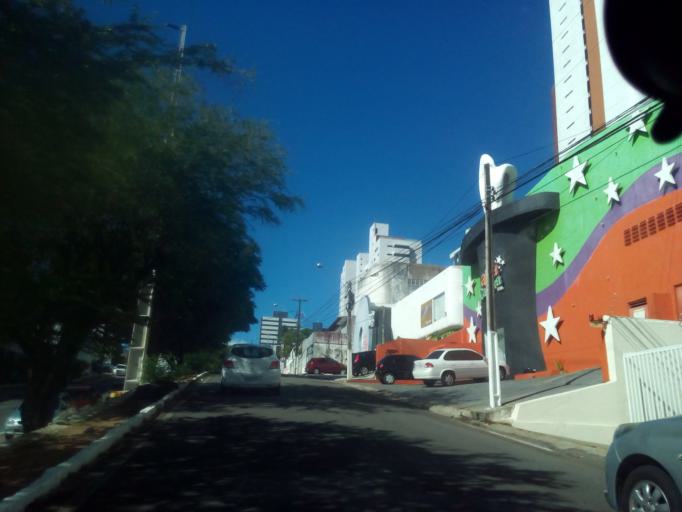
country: BR
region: Rio Grande do Norte
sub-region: Natal
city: Natal
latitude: -5.8057
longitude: -35.2059
